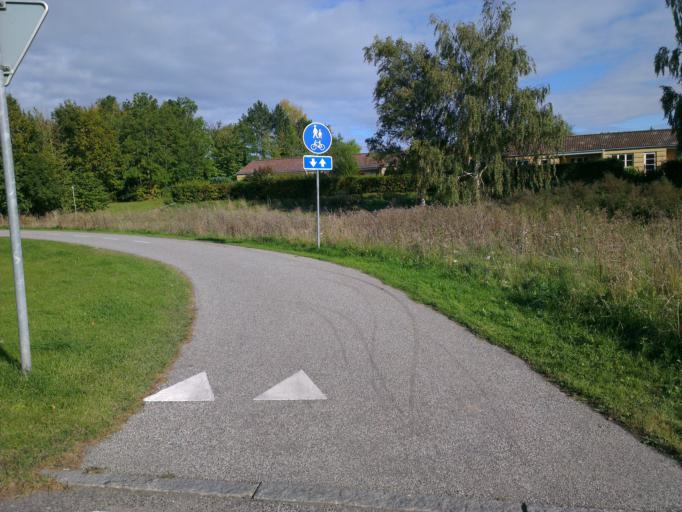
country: DK
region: Zealand
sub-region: Lejre Kommune
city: Ejby
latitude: 55.6869
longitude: 11.8519
